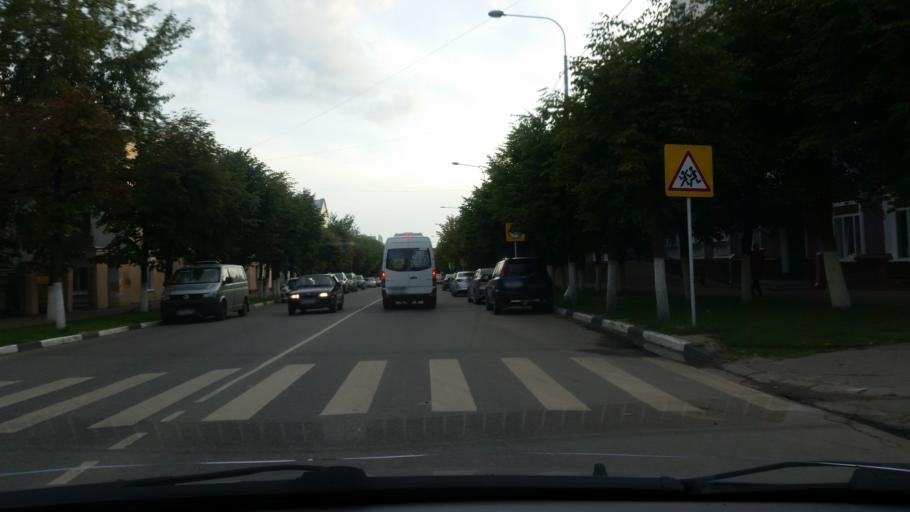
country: RU
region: Moskovskaya
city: Serpukhov
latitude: 54.9209
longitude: 37.4257
